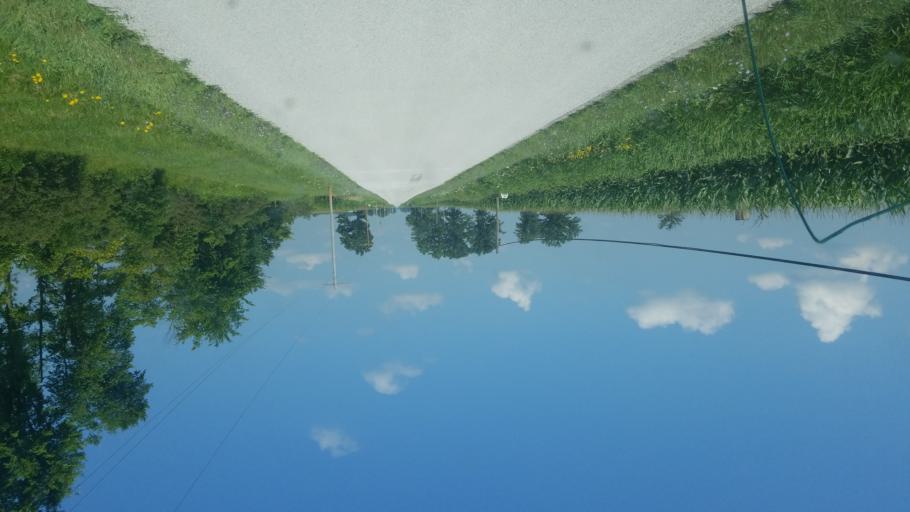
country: US
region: Ohio
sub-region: Hardin County
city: Ada
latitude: 40.6742
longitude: -83.7421
